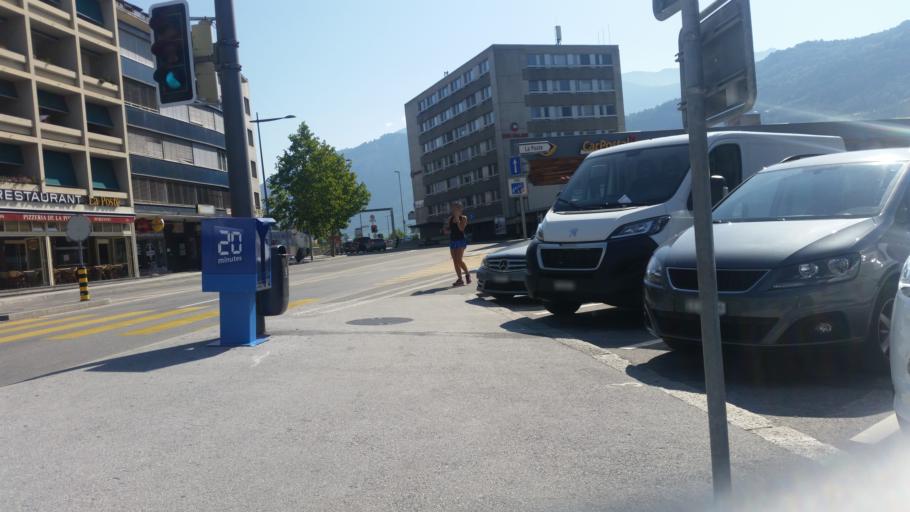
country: CH
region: Valais
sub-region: Sion District
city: Sitten
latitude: 46.2281
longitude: 7.3575
